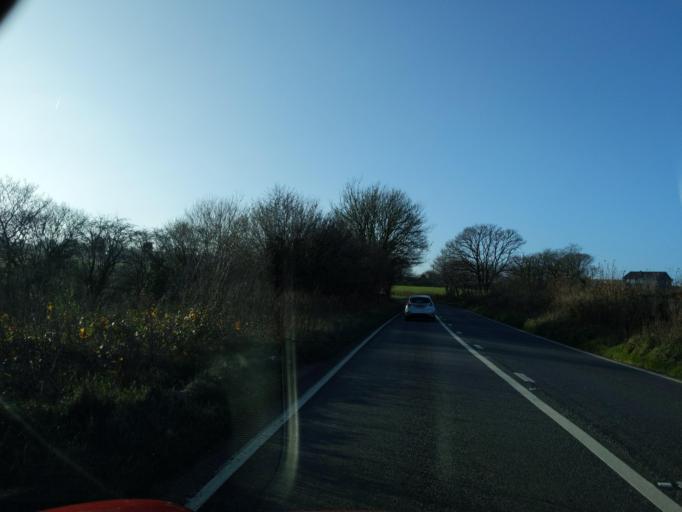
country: GB
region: England
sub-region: Cornwall
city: Liskeard
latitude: 50.4497
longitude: -4.5500
